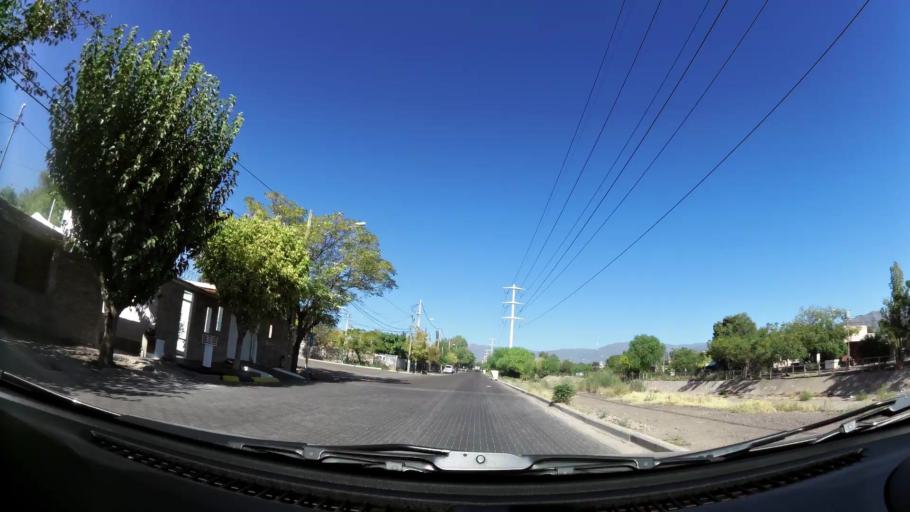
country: AR
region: Mendoza
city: Las Heras
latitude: -32.8718
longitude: -68.8660
